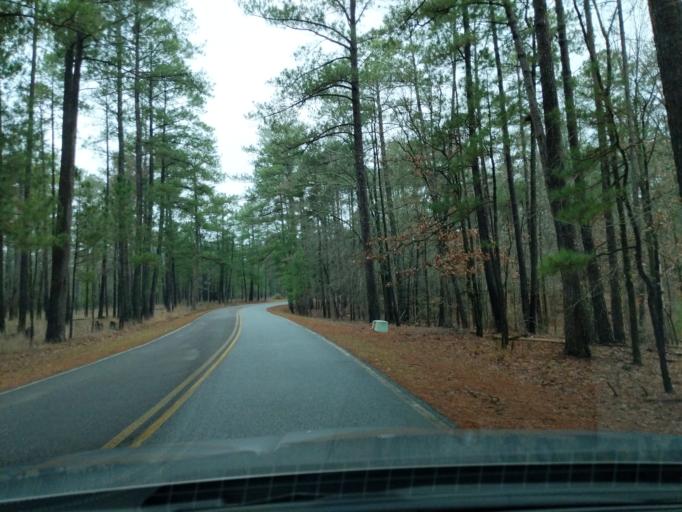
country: US
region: Georgia
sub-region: Columbia County
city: Appling
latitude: 33.6485
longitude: -82.3772
